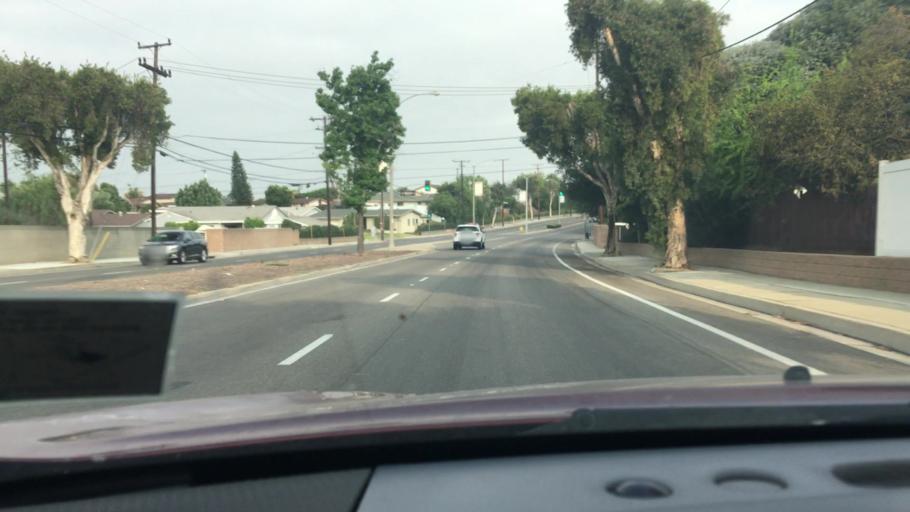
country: US
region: California
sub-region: Los Angeles County
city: La Mirada
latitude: 33.8985
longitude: -118.0137
